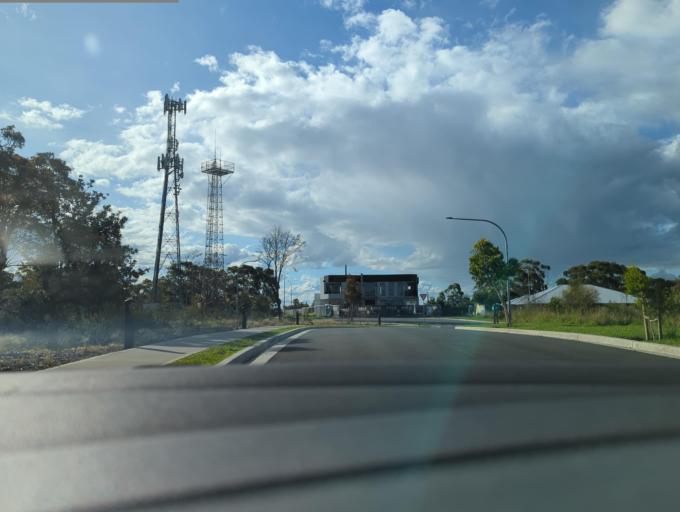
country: AU
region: New South Wales
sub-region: Sutherland Shire
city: Woronora Heights
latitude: -34.0399
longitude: 150.9998
